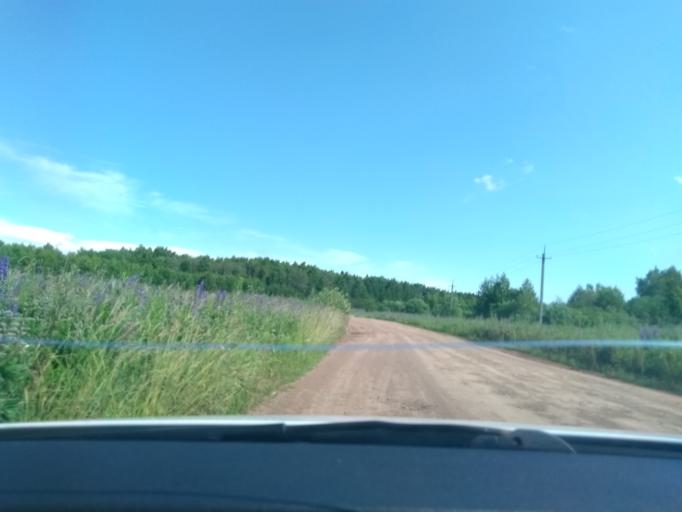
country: RU
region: Perm
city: Sylva
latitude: 57.8251
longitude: 56.7471
